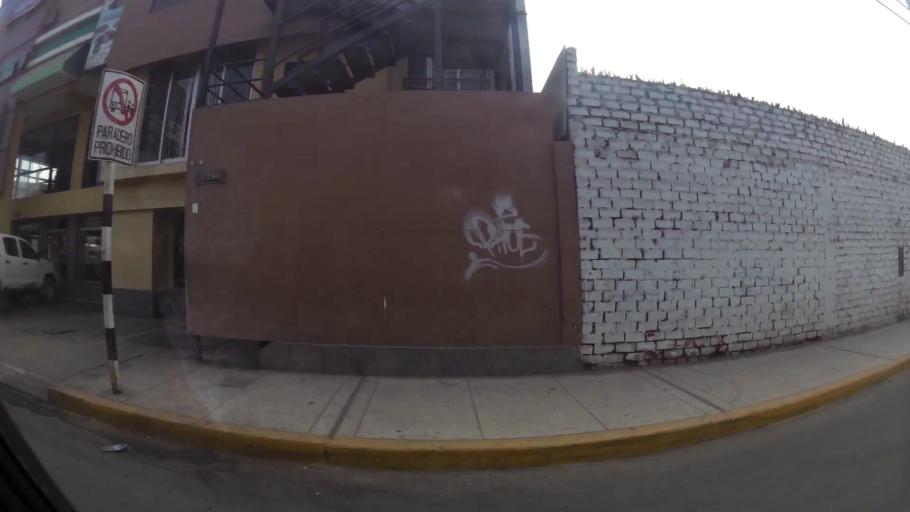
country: PE
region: La Libertad
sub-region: Provincia de Trujillo
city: Trujillo
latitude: -8.1225
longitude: -79.0222
